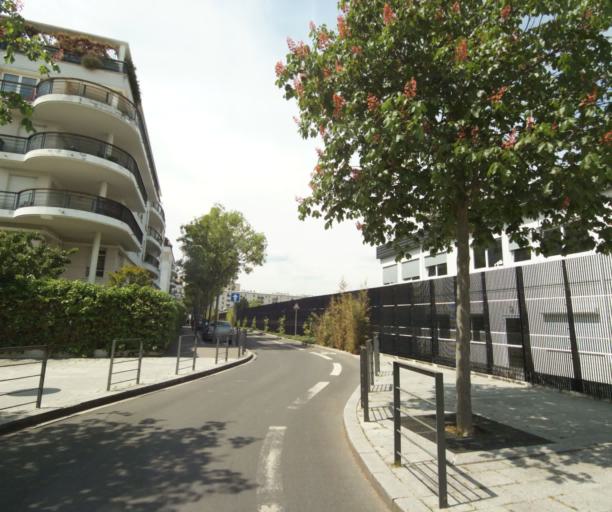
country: FR
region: Ile-de-France
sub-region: Departement des Hauts-de-Seine
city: Colombes
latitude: 48.9091
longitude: 2.2602
